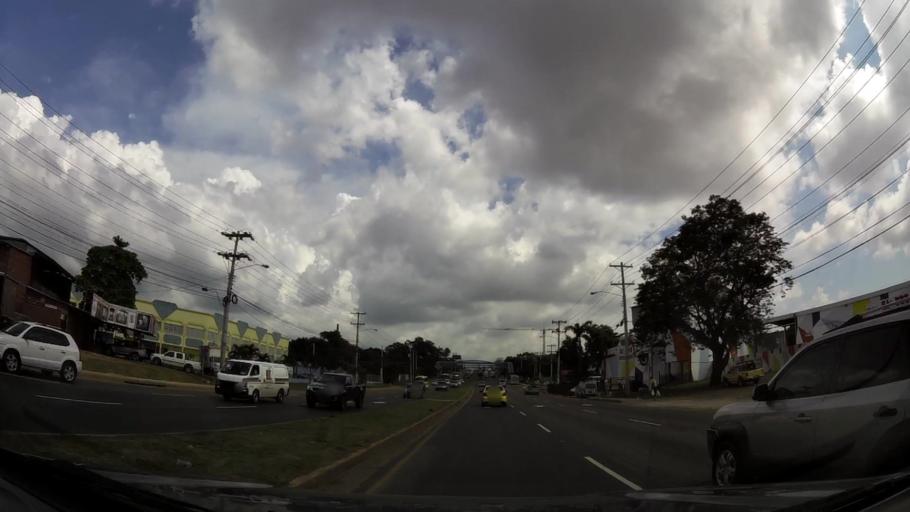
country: PA
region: Panama
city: San Miguelito
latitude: 9.0546
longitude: -79.4392
